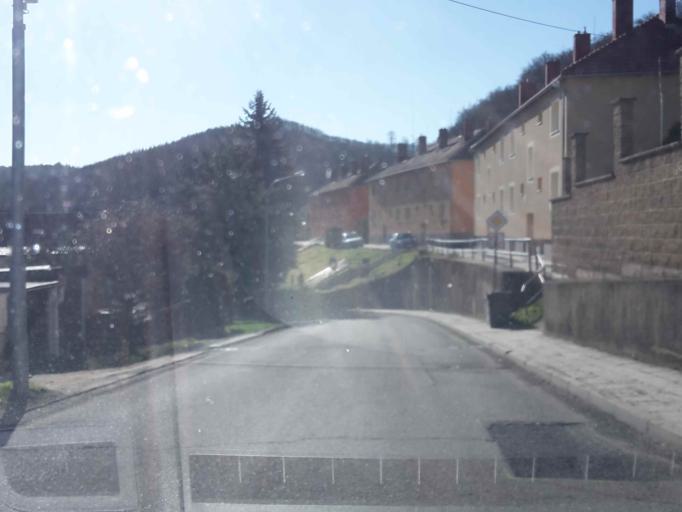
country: CZ
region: South Moravian
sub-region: Okres Blansko
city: Adamov
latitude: 49.2929
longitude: 16.6655
